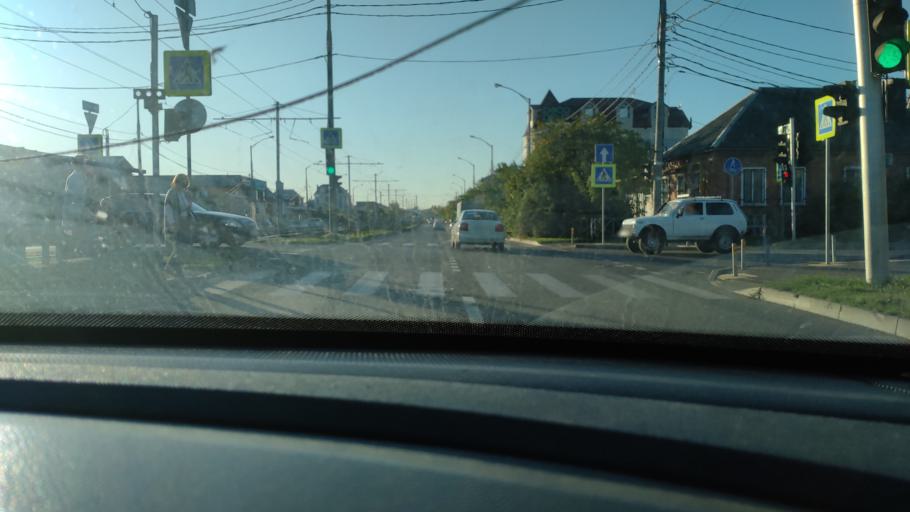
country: RU
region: Krasnodarskiy
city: Krasnodar
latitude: 45.0423
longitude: 38.9427
